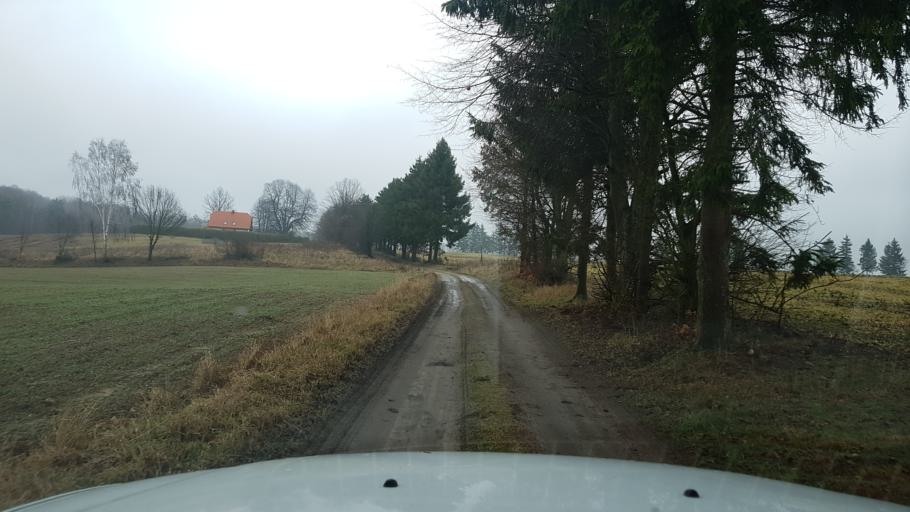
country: PL
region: West Pomeranian Voivodeship
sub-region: Powiat drawski
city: Czaplinek
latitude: 53.5774
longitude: 16.2672
